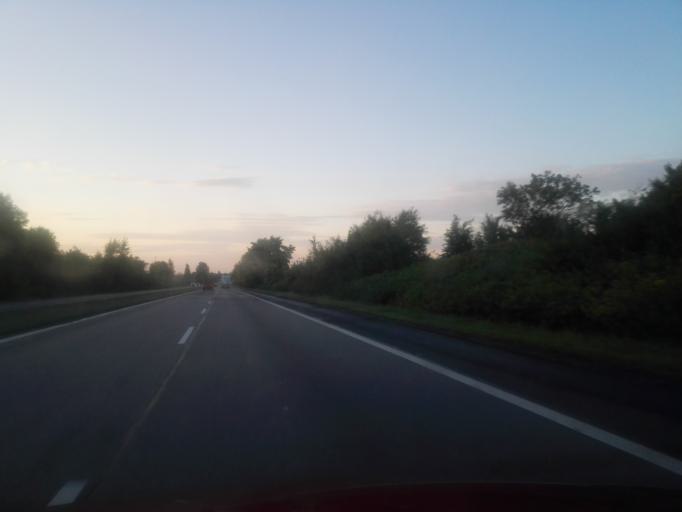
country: PL
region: Silesian Voivodeship
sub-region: Powiat czestochowski
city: Redziny
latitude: 50.8580
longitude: 19.1533
